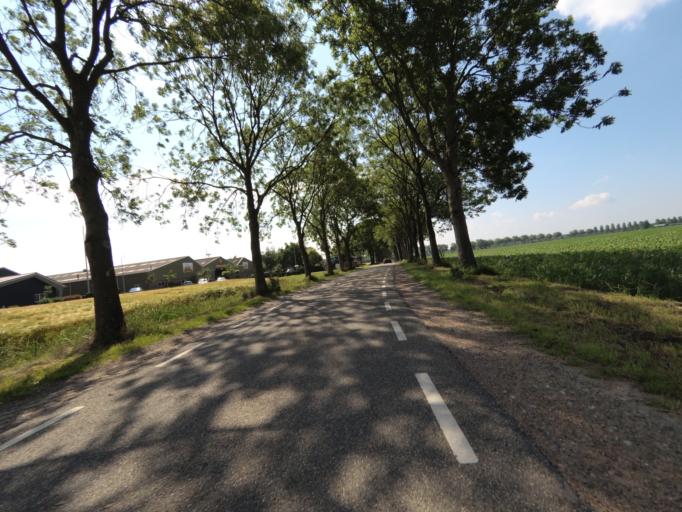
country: NL
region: Gelderland
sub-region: Gemeente Culemborg
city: Culemborg
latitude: 51.9407
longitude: 5.1818
